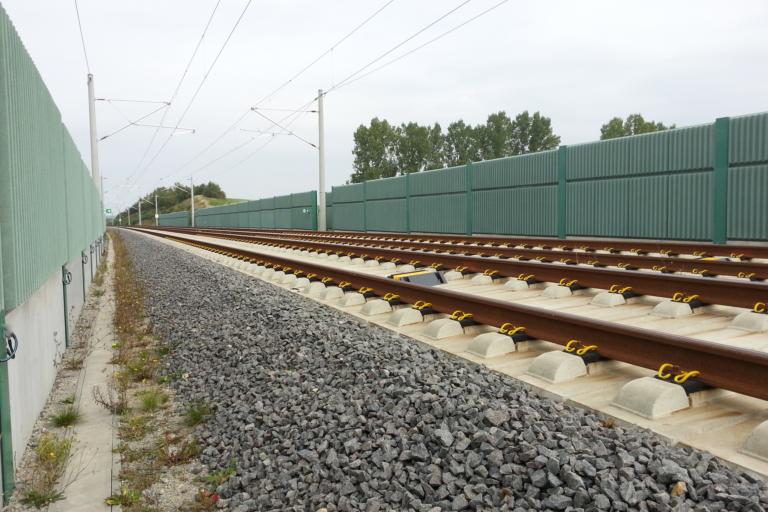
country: DE
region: Thuringia
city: Langewiesen
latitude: 50.7015
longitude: 11.0056
